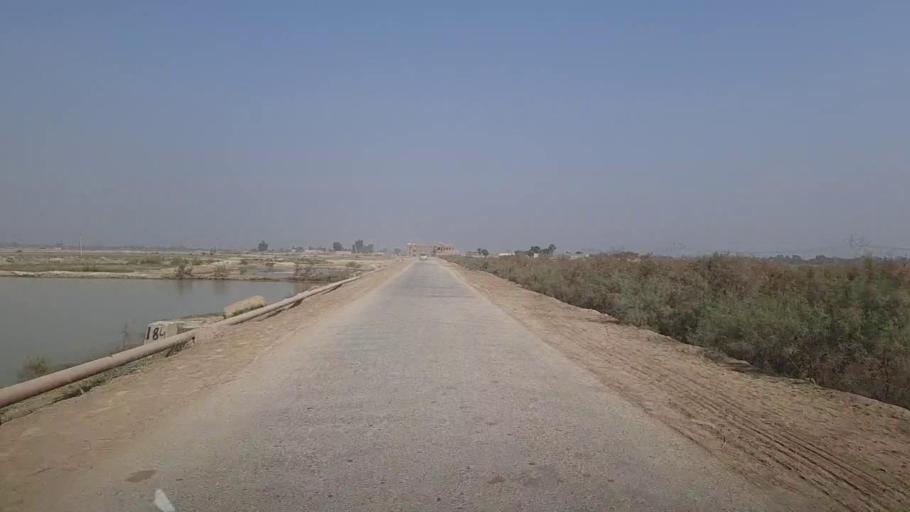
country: PK
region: Sindh
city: Kandhkot
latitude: 28.2267
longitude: 69.2053
